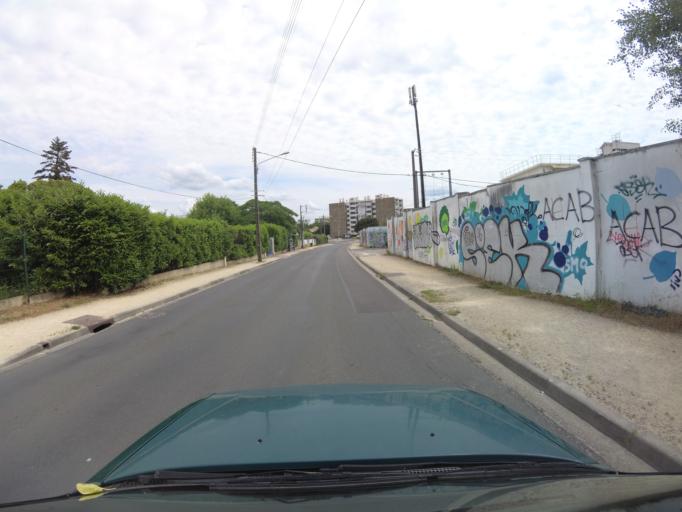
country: FR
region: Aquitaine
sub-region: Departement de la Gironde
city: Talence
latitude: 44.7968
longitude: -0.6105
